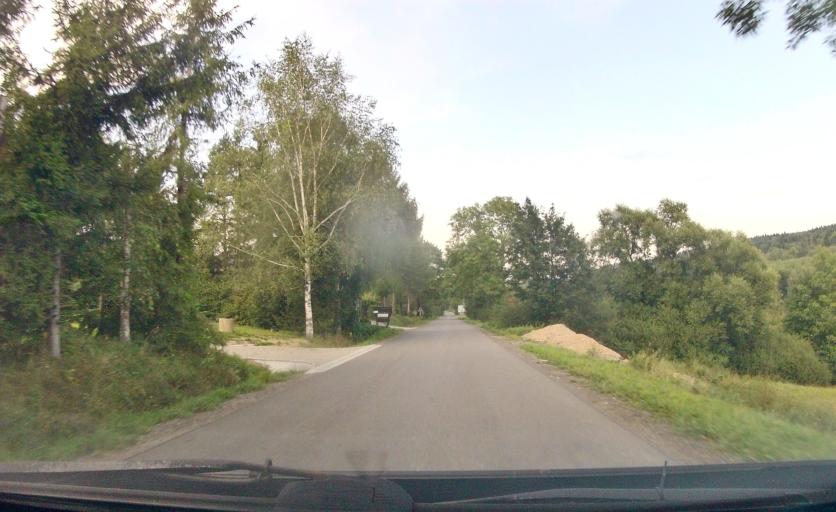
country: PL
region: Subcarpathian Voivodeship
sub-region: Powiat krosnienski
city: Dukla
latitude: 49.5353
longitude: 21.6154
